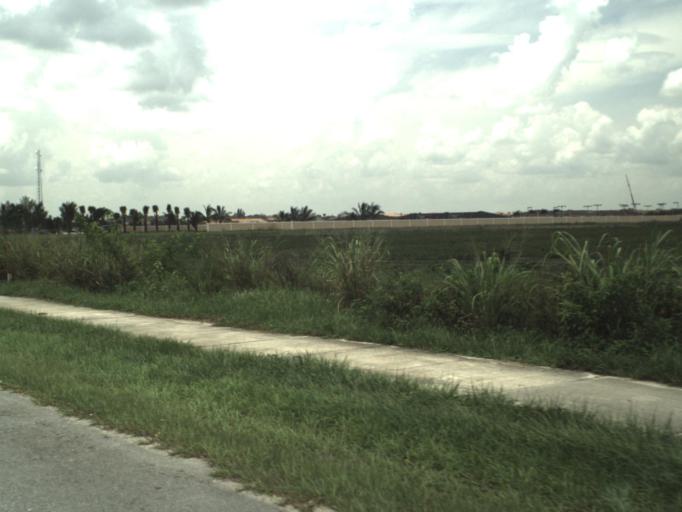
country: US
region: Florida
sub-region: Palm Beach County
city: Villages of Oriole
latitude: 26.4538
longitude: -80.1645
